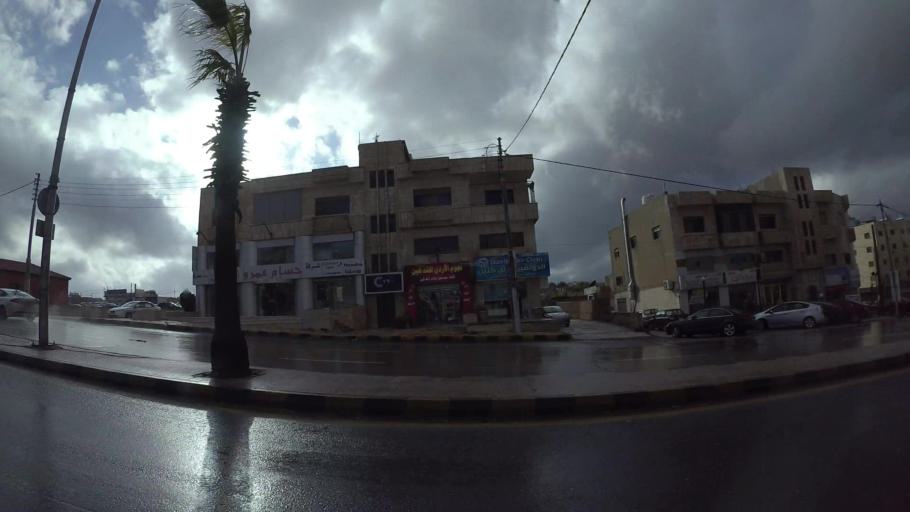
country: JO
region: Amman
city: Al Jubayhah
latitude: 32.0299
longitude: 35.8631
